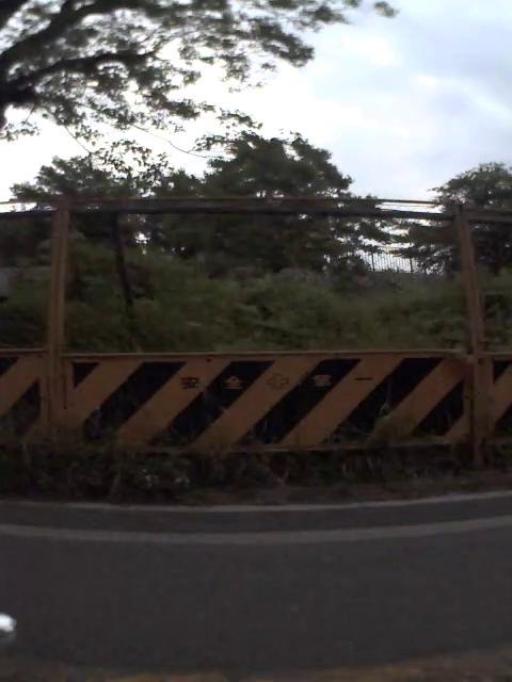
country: JP
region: Osaka
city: Hirakata
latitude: 34.7980
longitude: 135.6465
